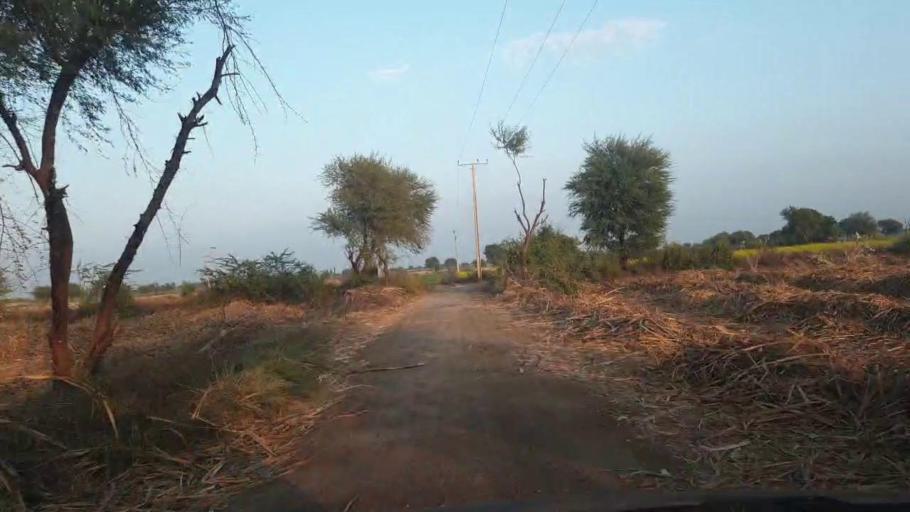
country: PK
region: Sindh
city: Berani
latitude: 25.8462
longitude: 68.7443
